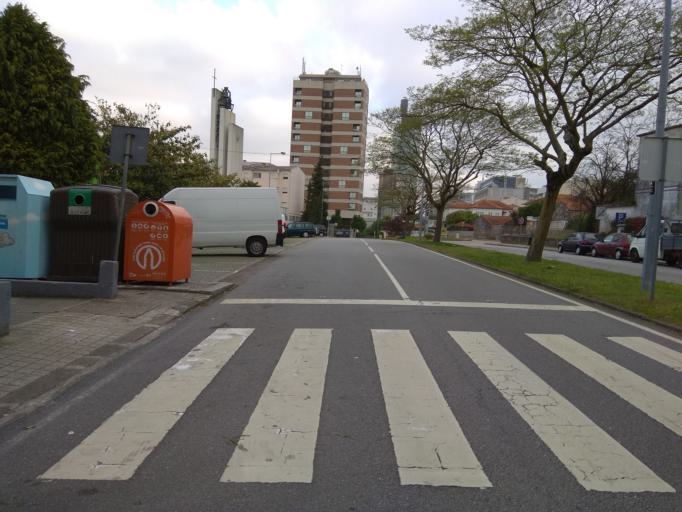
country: PT
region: Porto
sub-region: Maia
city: Maia
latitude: 41.2300
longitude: -8.6210
